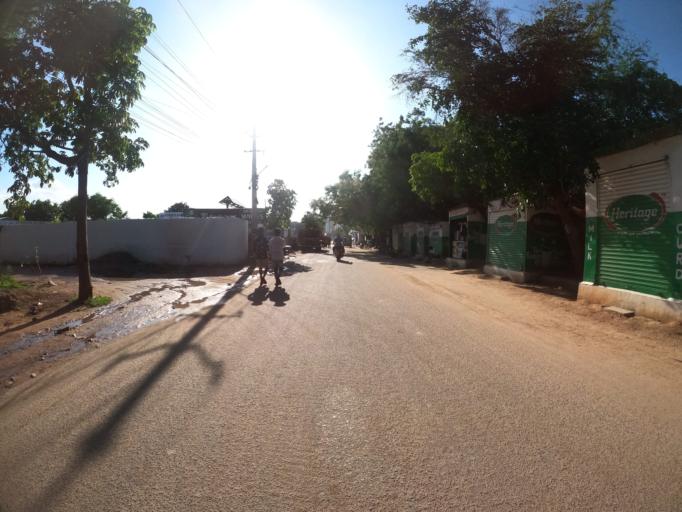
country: IN
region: Telangana
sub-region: Hyderabad
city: Hyderabad
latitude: 17.3548
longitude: 78.3782
